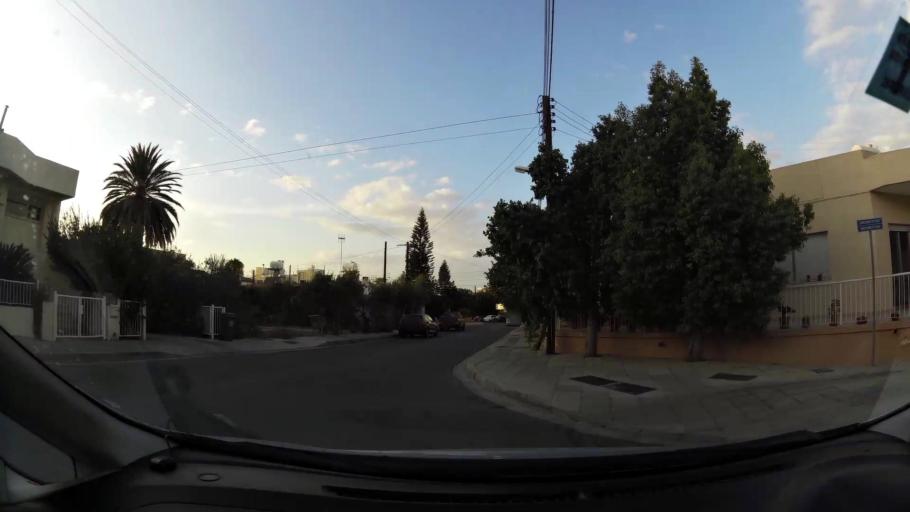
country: CY
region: Lefkosia
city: Nicosia
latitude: 35.1572
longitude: 33.4002
